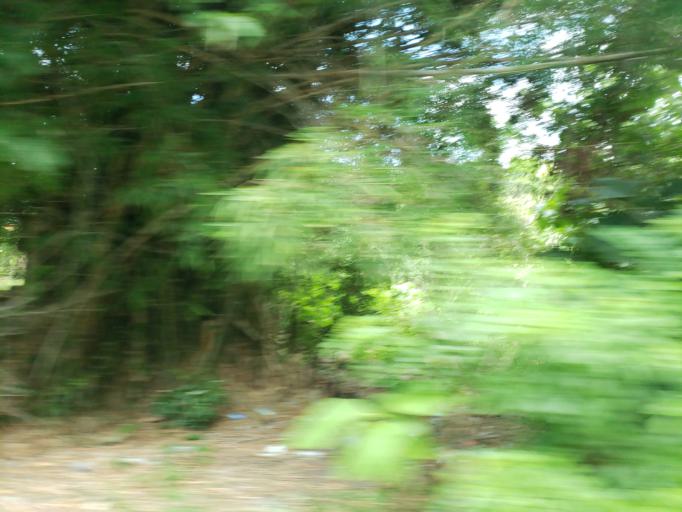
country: ID
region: Bali
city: Pecatu
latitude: -8.8379
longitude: 115.1254
